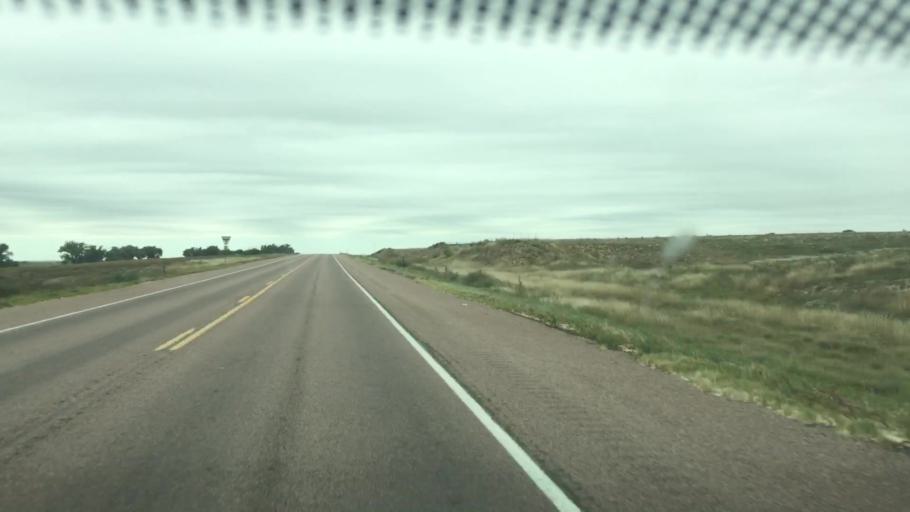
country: US
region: Kansas
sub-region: Hamilton County
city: Syracuse
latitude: 38.0521
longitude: -102.0636
